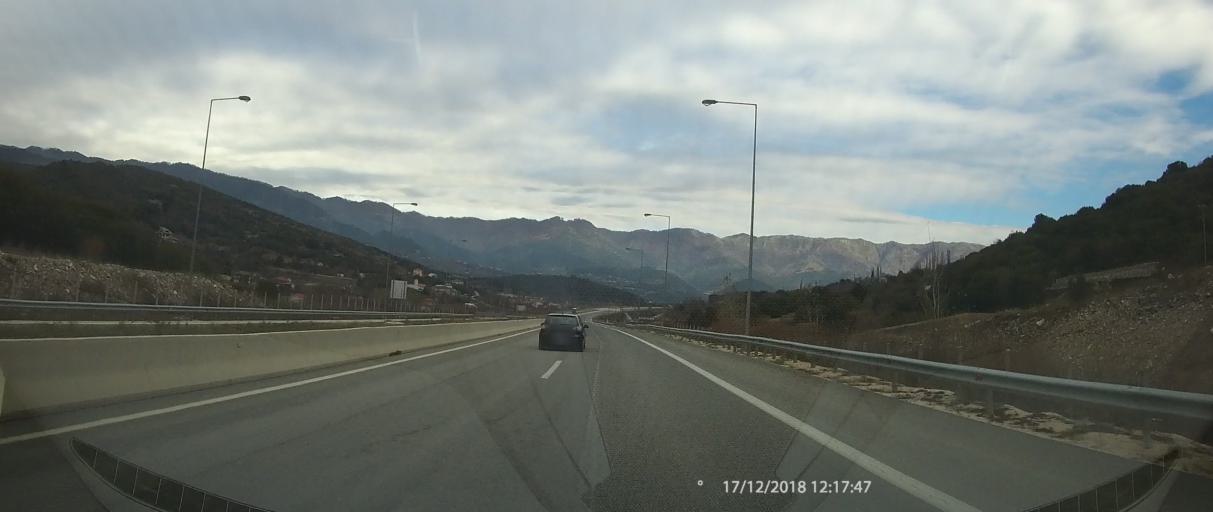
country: GR
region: Epirus
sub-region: Nomos Ioanninon
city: Metsovo
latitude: 39.7435
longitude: 21.0707
